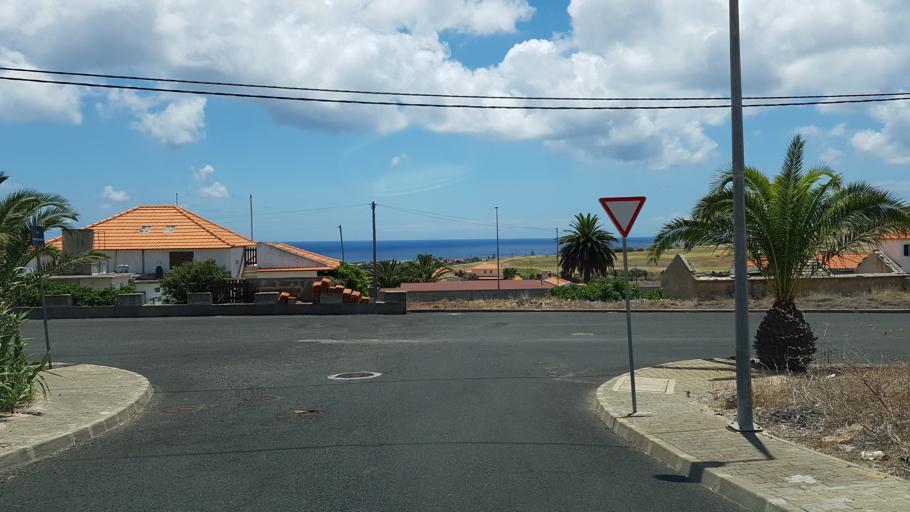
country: PT
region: Madeira
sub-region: Porto Santo
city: Vila de Porto Santo
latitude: 33.0562
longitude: -16.3622
